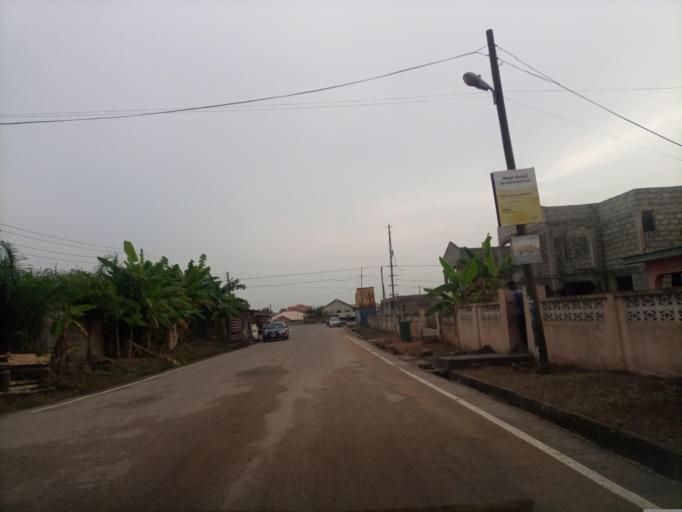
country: GH
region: Western
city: Takoradi
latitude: 4.9285
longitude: -1.7827
